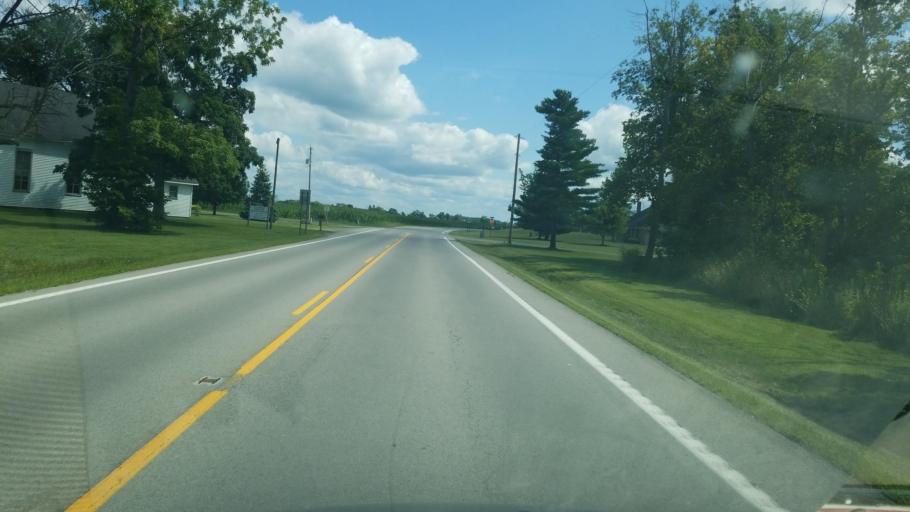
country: US
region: Ohio
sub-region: Putnam County
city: Kalida
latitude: 40.9481
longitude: -84.1637
